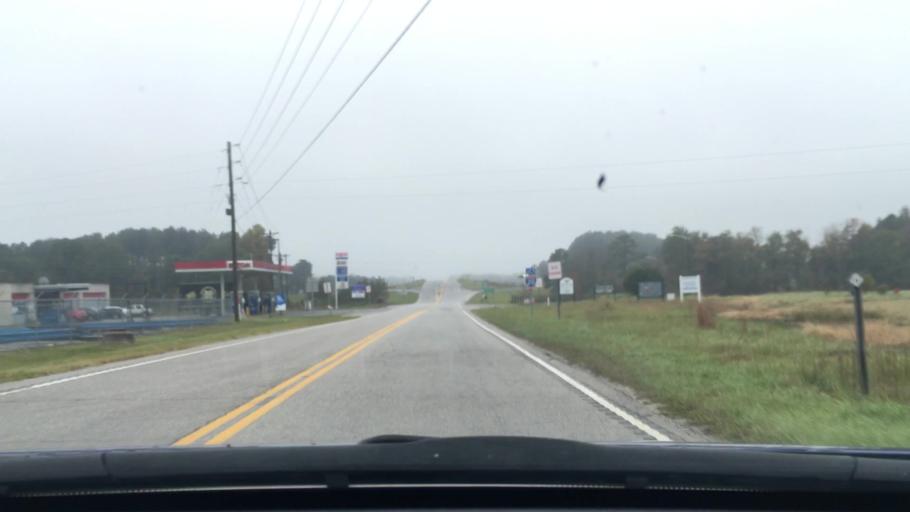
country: US
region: South Carolina
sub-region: Florence County
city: Timmonsville
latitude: 34.2090
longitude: -80.0223
